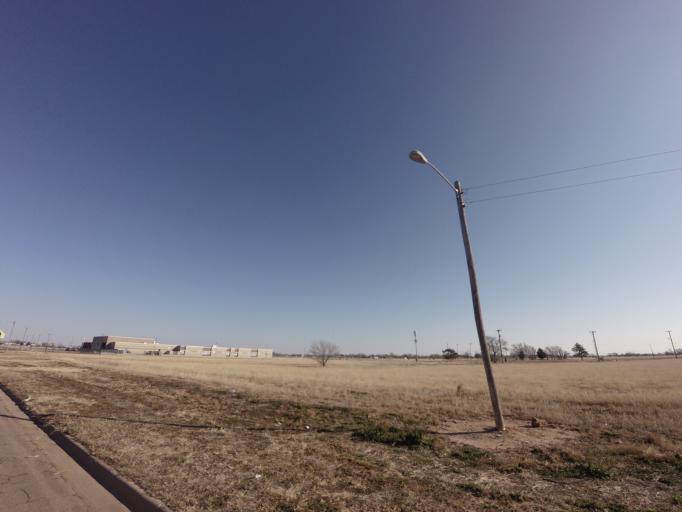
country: US
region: New Mexico
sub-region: Curry County
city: Clovis
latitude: 34.3837
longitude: -103.1938
